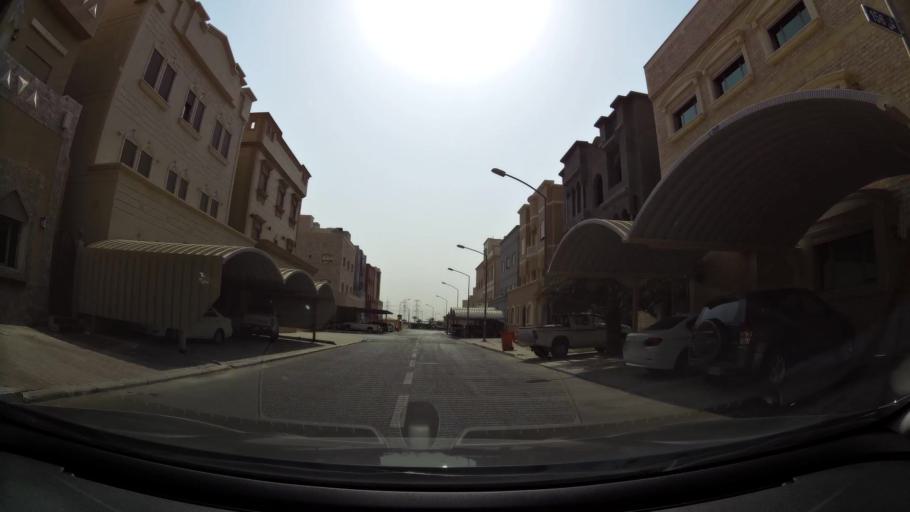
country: KW
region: Muhafazat al Jahra'
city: Al Jahra'
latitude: 29.3327
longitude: 47.7796
